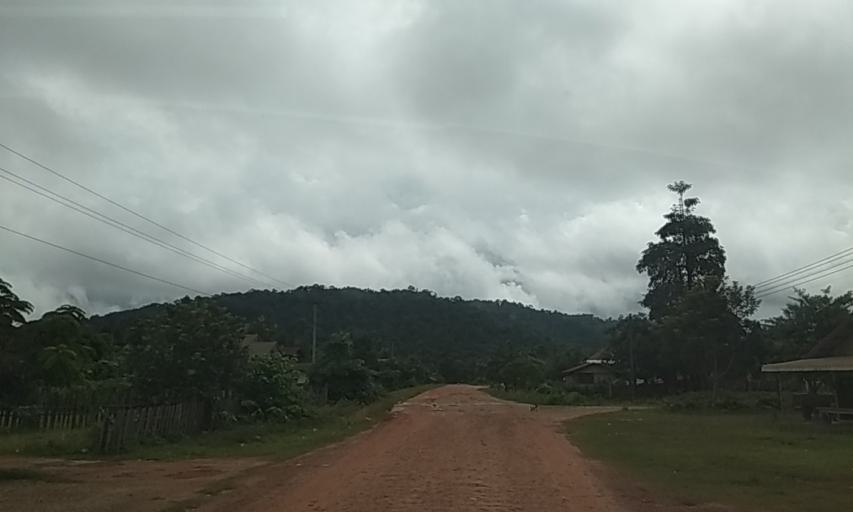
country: LA
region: Bolikhamxai
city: Bolikhan
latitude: 18.5571
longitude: 103.7382
